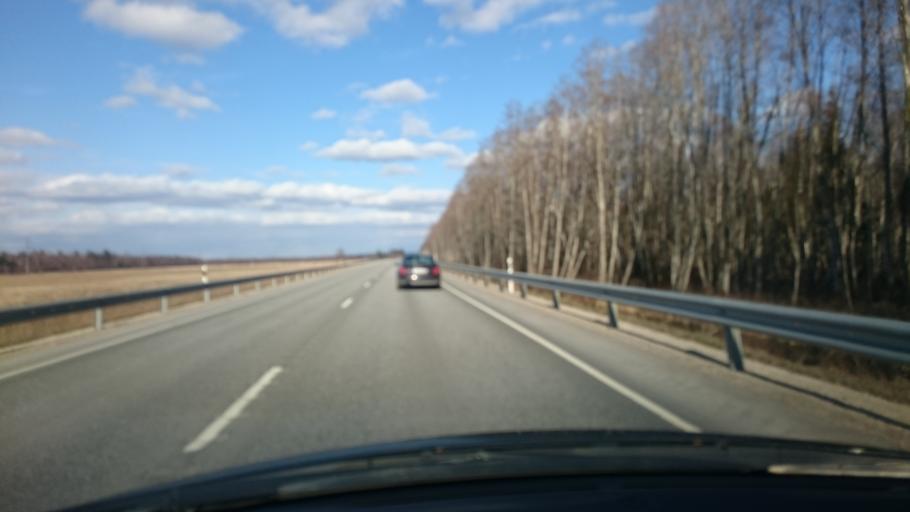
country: EE
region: Laeaene
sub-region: Lihula vald
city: Lihula
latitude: 58.7838
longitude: 24.0071
